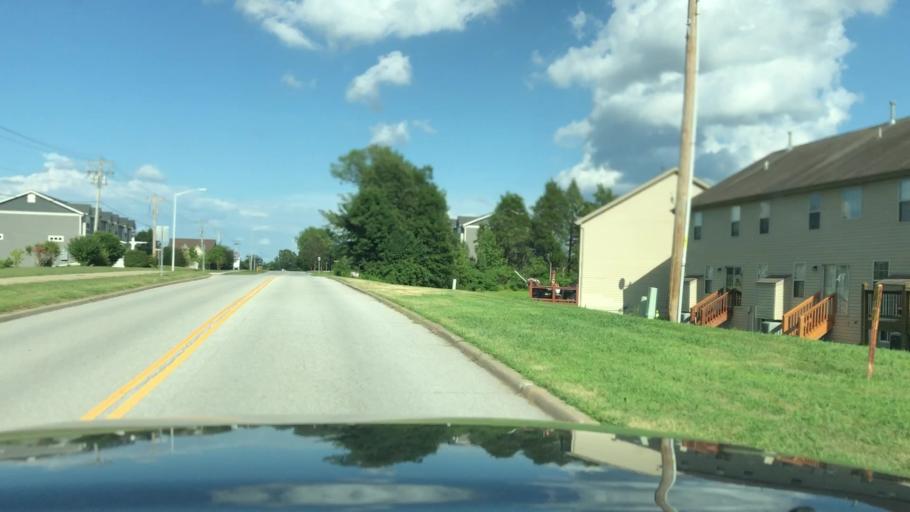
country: US
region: Missouri
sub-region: Saint Charles County
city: Lake Saint Louis
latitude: 38.7959
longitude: -90.8138
